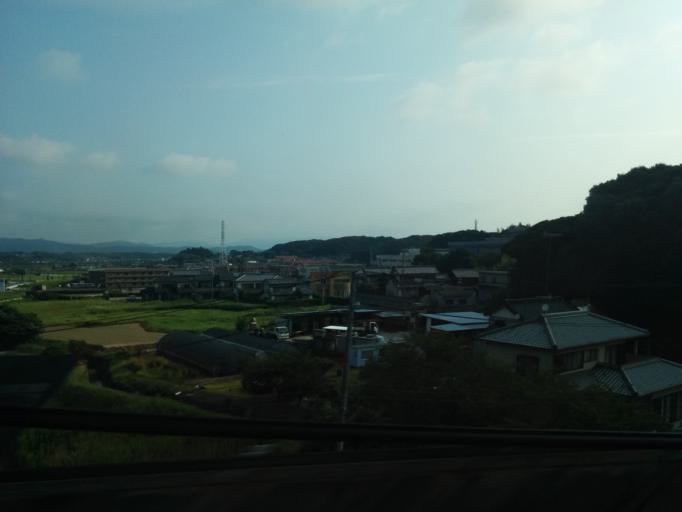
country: JP
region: Shizuoka
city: Kosai-shi
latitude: 34.7063
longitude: 137.5222
